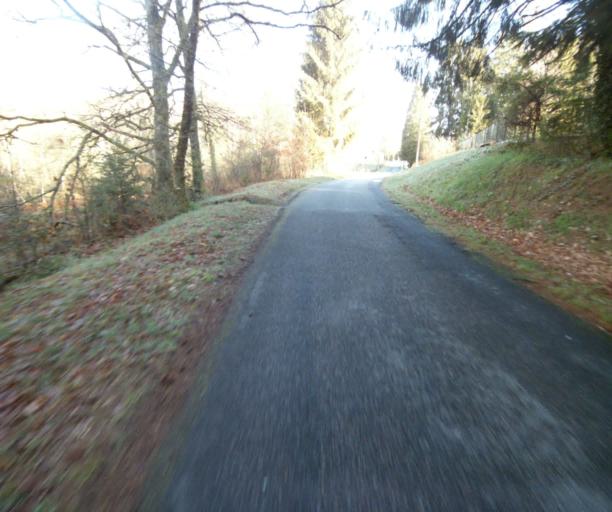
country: FR
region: Limousin
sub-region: Departement de la Correze
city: Correze
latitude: 45.2848
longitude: 1.8660
